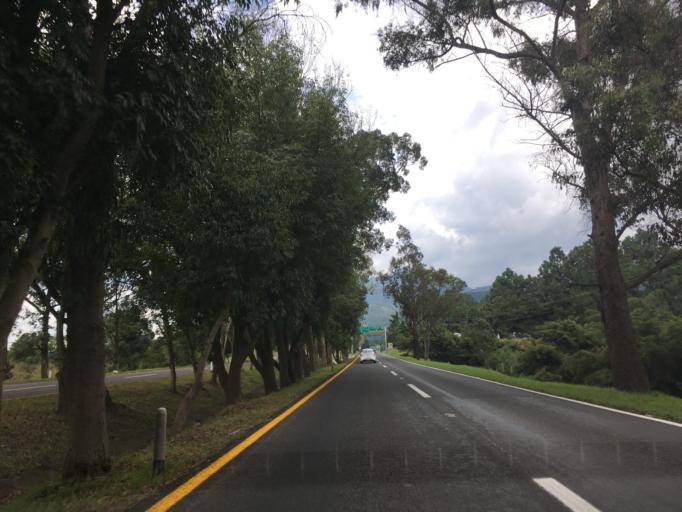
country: MX
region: Michoacan
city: Patzcuaro
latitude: 19.5357
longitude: -101.5715
